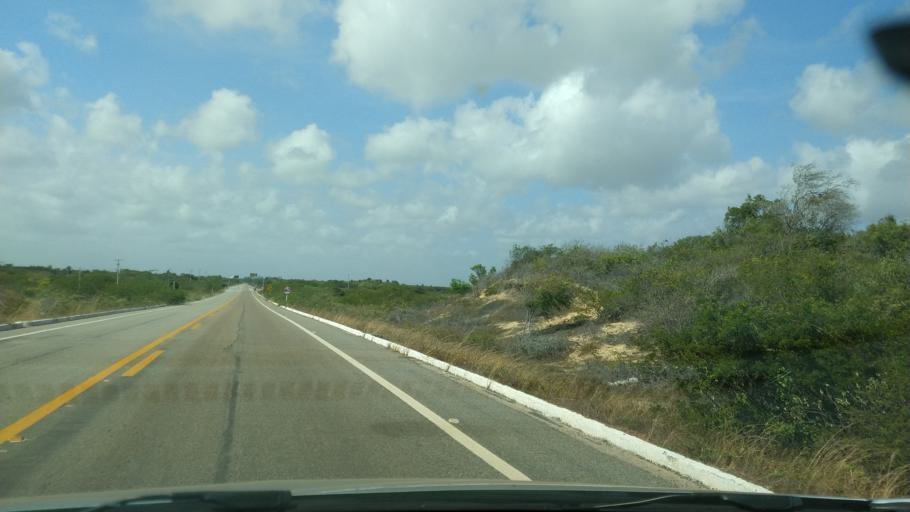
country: BR
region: Rio Grande do Norte
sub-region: Touros
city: Touros
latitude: -5.1695
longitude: -35.5057
